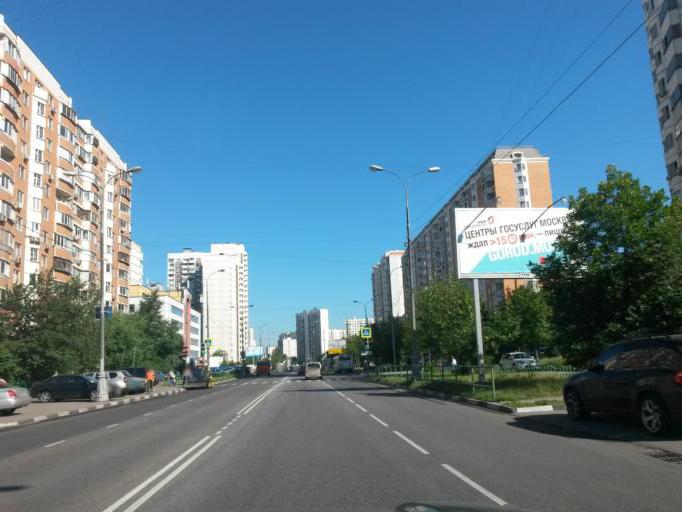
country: RU
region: Moscow
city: Lyublino
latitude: 55.6636
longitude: 37.7717
